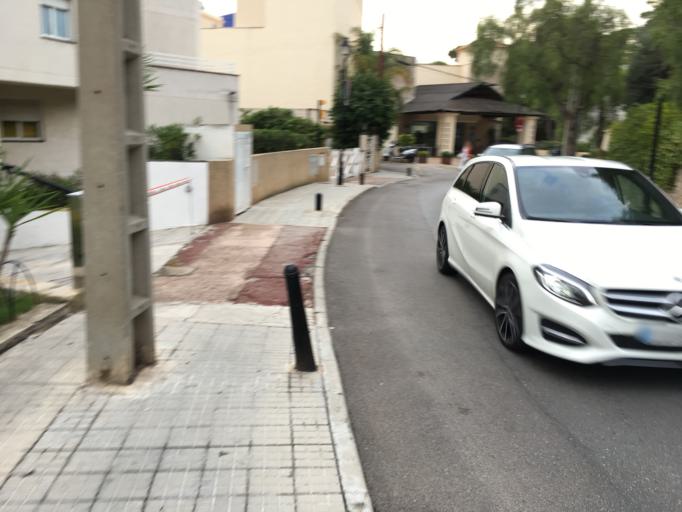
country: ES
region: Balearic Islands
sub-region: Illes Balears
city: Palma
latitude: 39.5401
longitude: 2.5934
